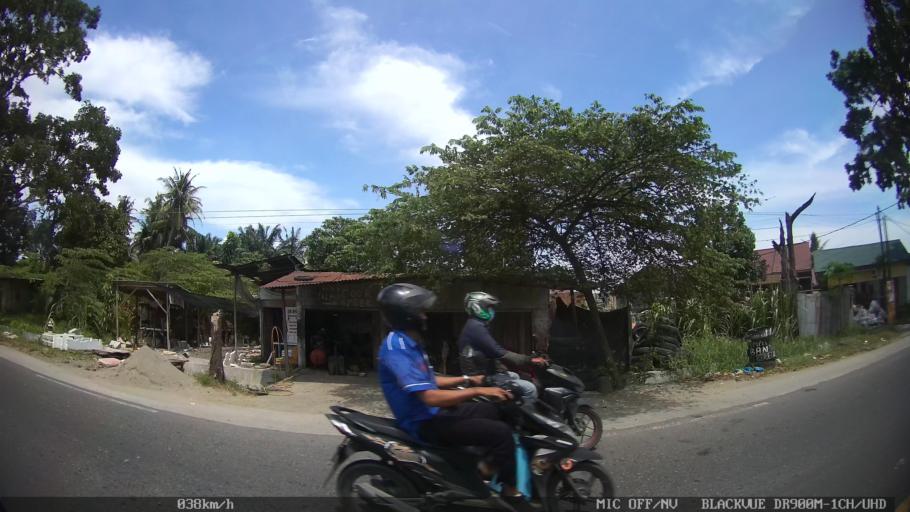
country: ID
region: North Sumatra
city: Binjai
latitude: 3.6296
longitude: 98.5102
